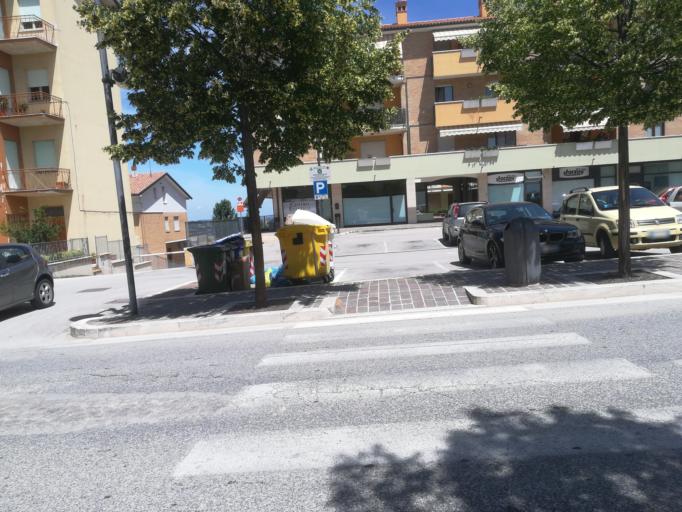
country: IT
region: The Marches
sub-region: Provincia di Macerata
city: Mogliano
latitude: 43.1858
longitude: 13.4735
